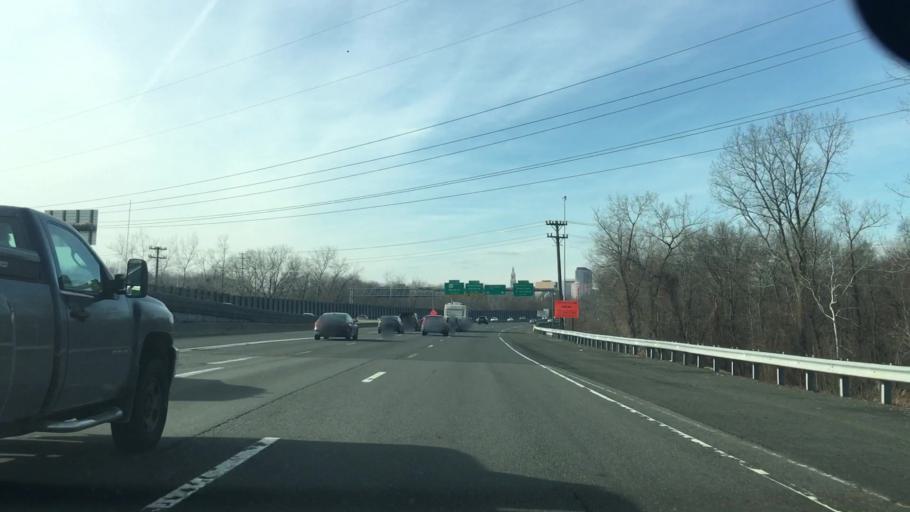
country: US
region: Connecticut
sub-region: Hartford County
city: East Hartford
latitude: 41.7636
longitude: -72.6386
